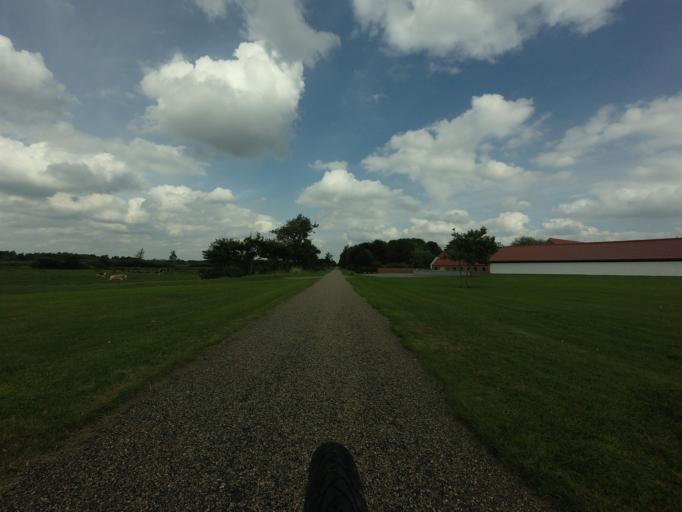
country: DK
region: Central Jutland
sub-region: Herning Kommune
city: Sunds
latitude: 56.2092
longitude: 9.0381
